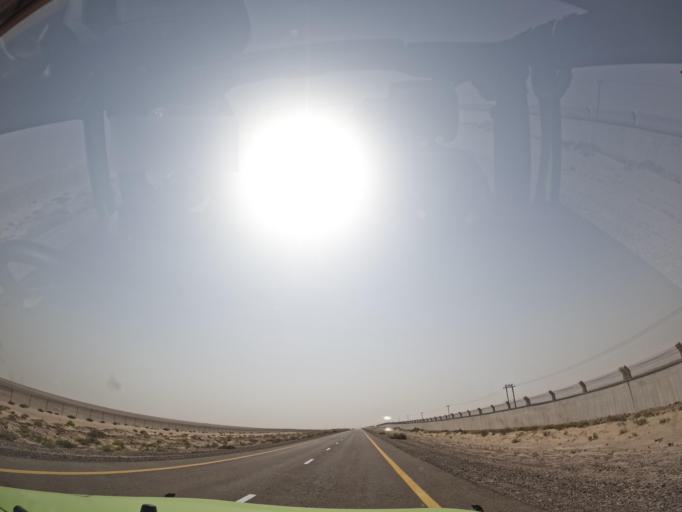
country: AE
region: Dubai
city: Dubai
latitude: 24.6285
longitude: 55.2666
